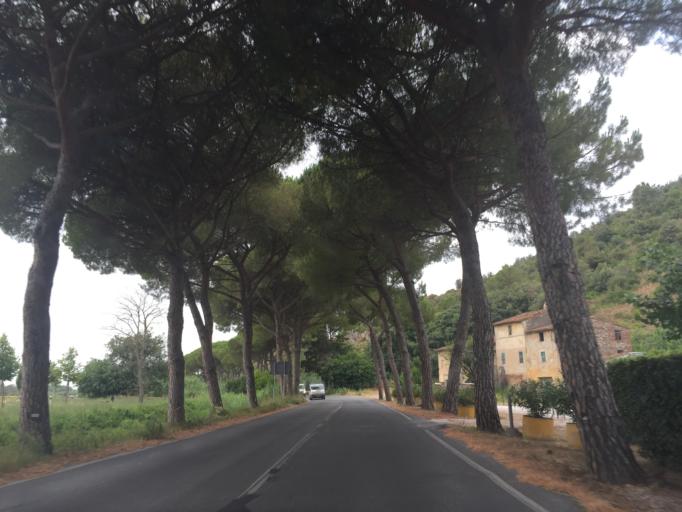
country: IT
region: Tuscany
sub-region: Province of Pisa
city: Uliveto Terme
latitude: 43.7012
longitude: 10.5137
